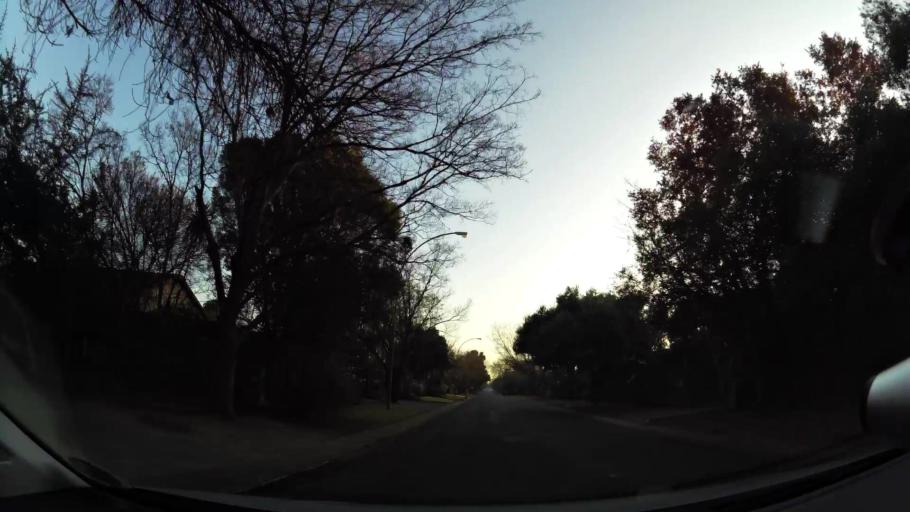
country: ZA
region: Orange Free State
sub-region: Mangaung Metropolitan Municipality
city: Bloemfontein
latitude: -29.1063
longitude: 26.1581
